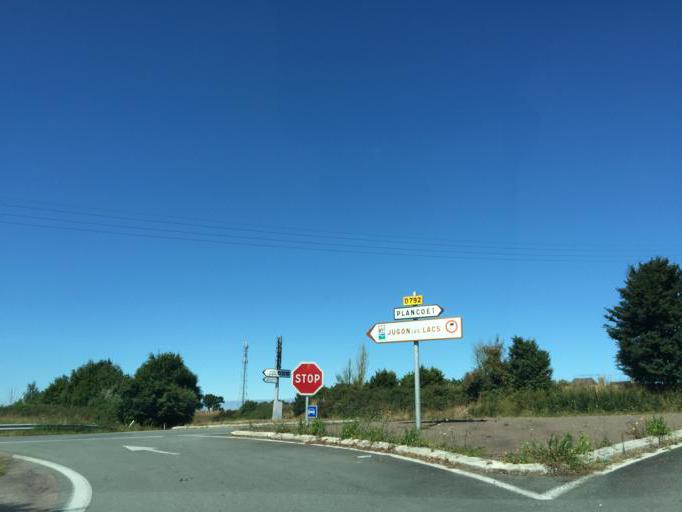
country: FR
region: Brittany
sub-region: Departement des Cotes-d'Armor
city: Jugon-les-Lacs
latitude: 48.4169
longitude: -2.3152
